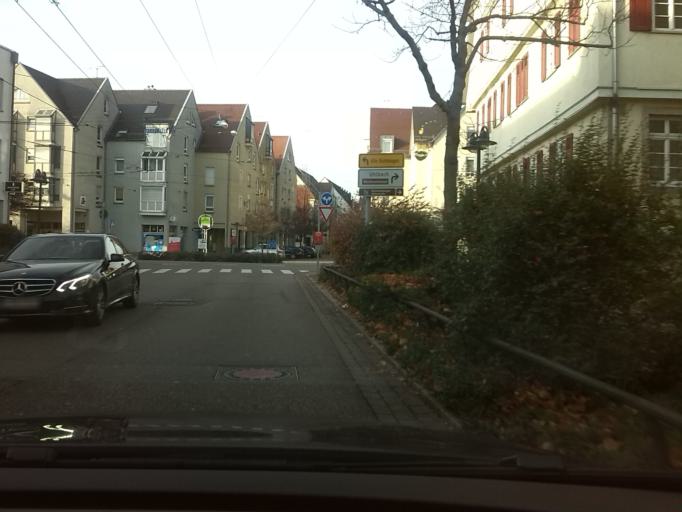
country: DE
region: Baden-Wuerttemberg
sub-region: Regierungsbezirk Stuttgart
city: Ostfildern
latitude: 48.7621
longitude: 9.2698
